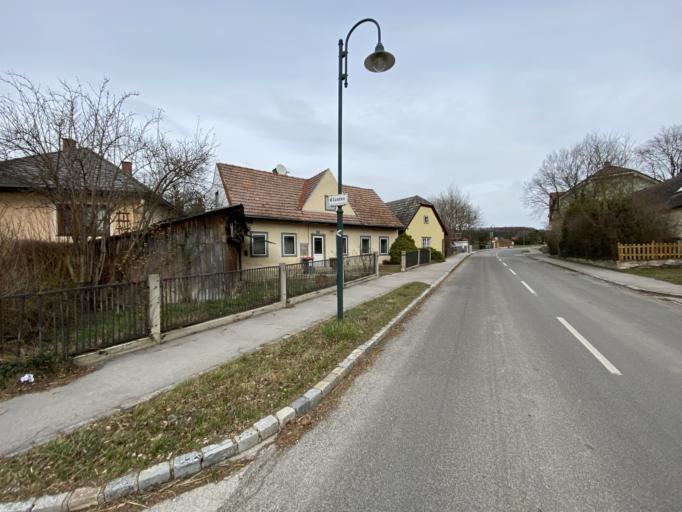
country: AT
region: Lower Austria
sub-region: Politischer Bezirk Modling
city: Gaaden
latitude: 48.0381
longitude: 16.1768
